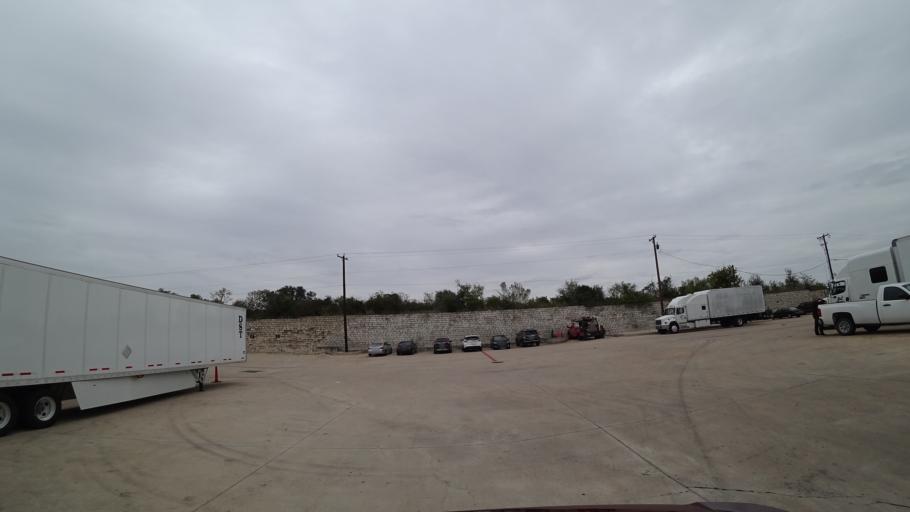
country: US
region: Texas
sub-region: Travis County
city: Wells Branch
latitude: 30.4492
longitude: -97.7066
